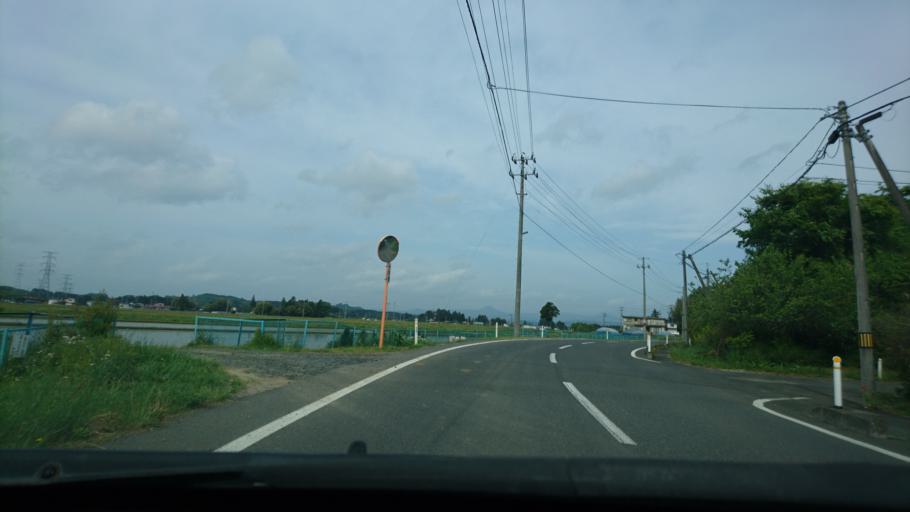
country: JP
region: Iwate
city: Ichinoseki
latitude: 38.8214
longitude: 141.0402
